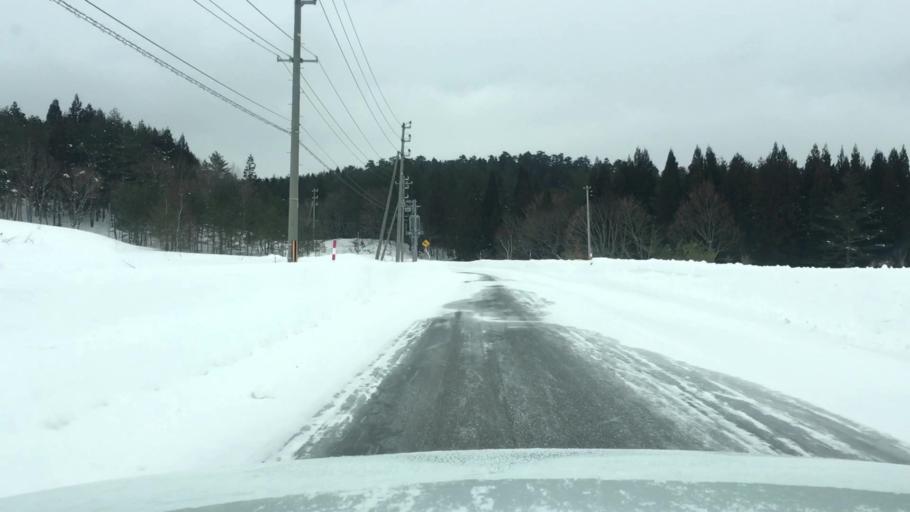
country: JP
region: Akita
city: Hanawa
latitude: 39.9933
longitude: 140.9956
